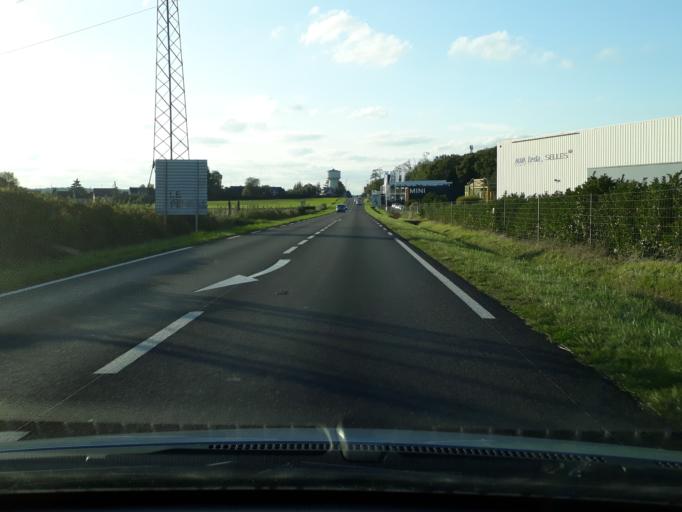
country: FR
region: Ile-de-France
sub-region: Departement de Seine-et-Marne
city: Vulaines-sur-Seine
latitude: 48.4234
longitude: 2.7669
